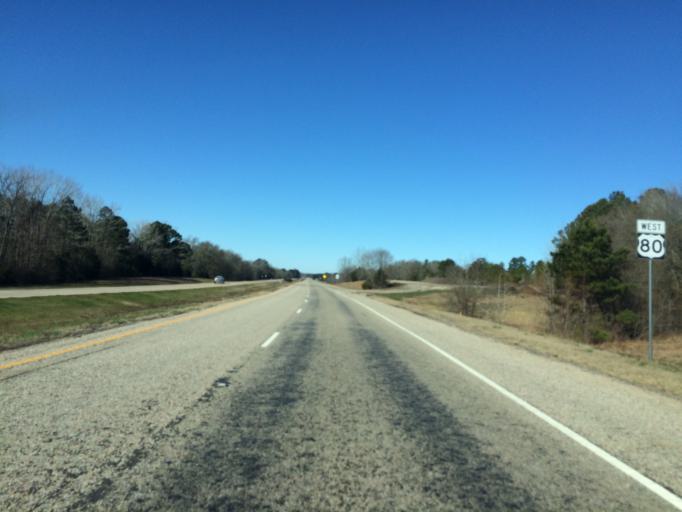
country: US
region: Texas
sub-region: Smith County
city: Lindale
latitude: 32.6271
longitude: -95.3363
